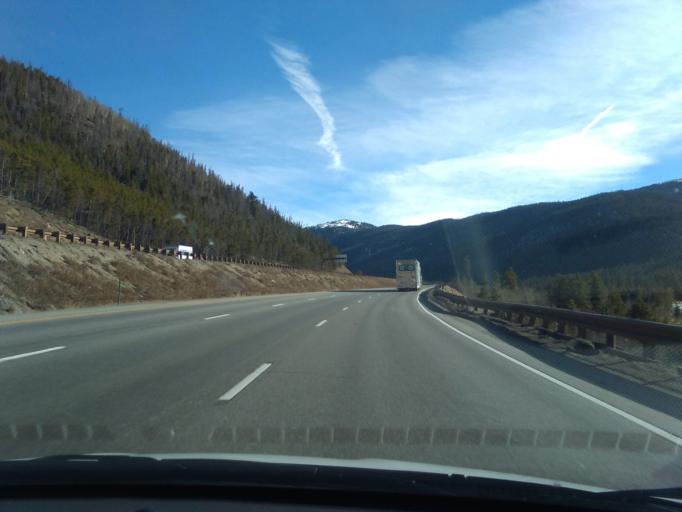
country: US
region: Colorado
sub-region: Summit County
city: Keystone
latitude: 39.6530
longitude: -106.0097
